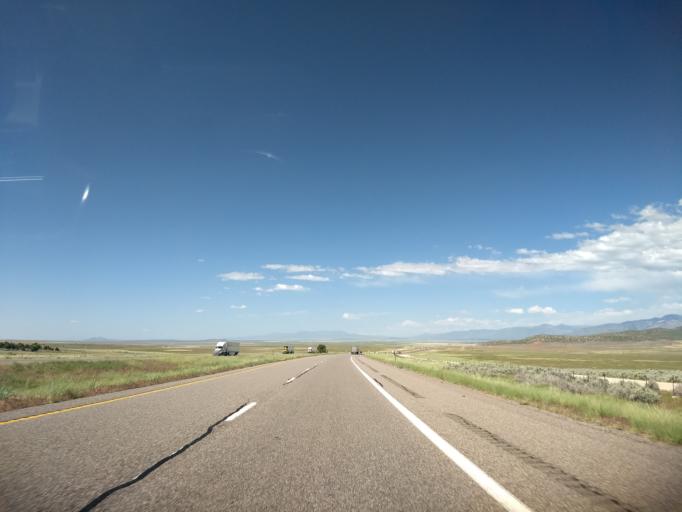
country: US
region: Utah
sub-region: Millard County
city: Fillmore
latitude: 38.7311
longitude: -112.5909
